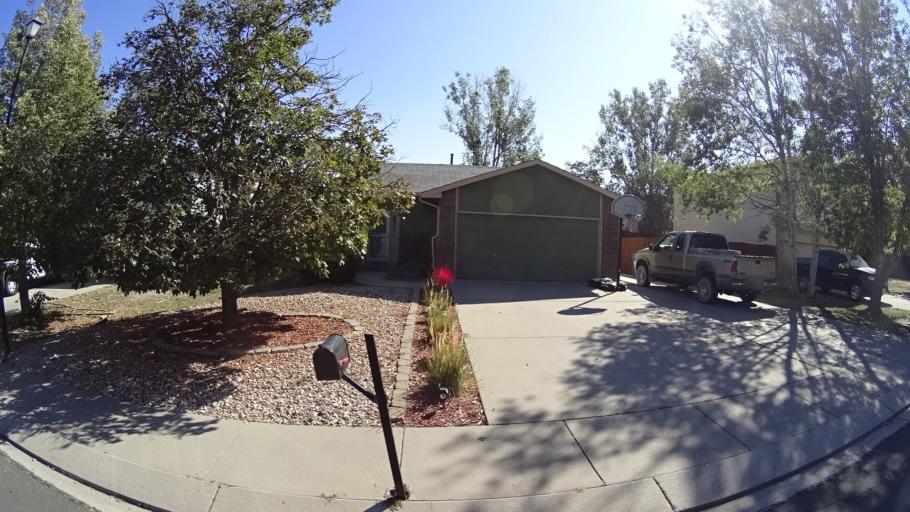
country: US
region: Colorado
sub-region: El Paso County
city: Cimarron Hills
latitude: 38.8734
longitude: -104.7064
